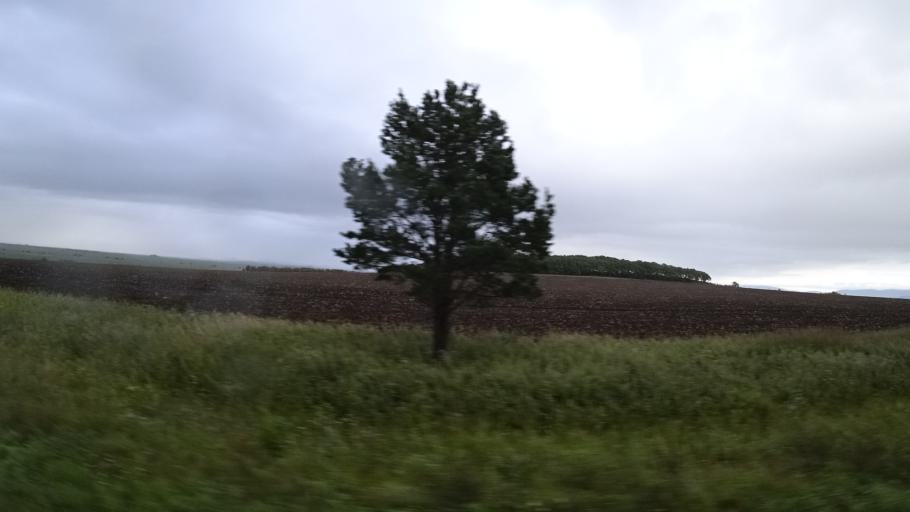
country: RU
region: Primorskiy
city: Chernigovka
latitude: 44.3689
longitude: 132.5323
